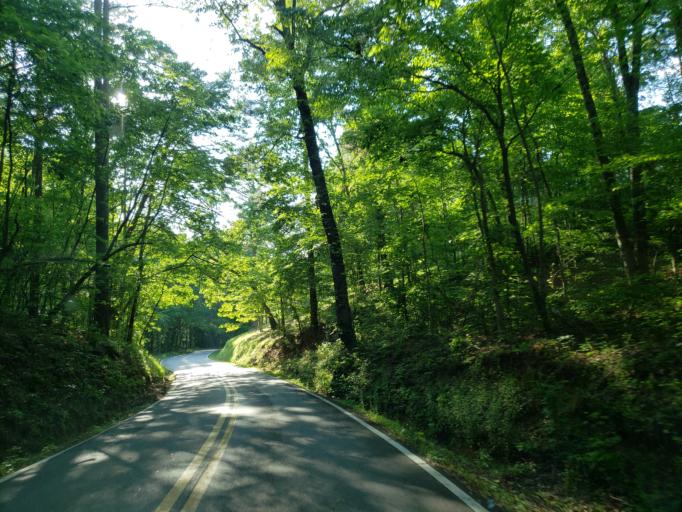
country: US
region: Georgia
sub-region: Murray County
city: Chatsworth
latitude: 34.6627
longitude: -84.6439
